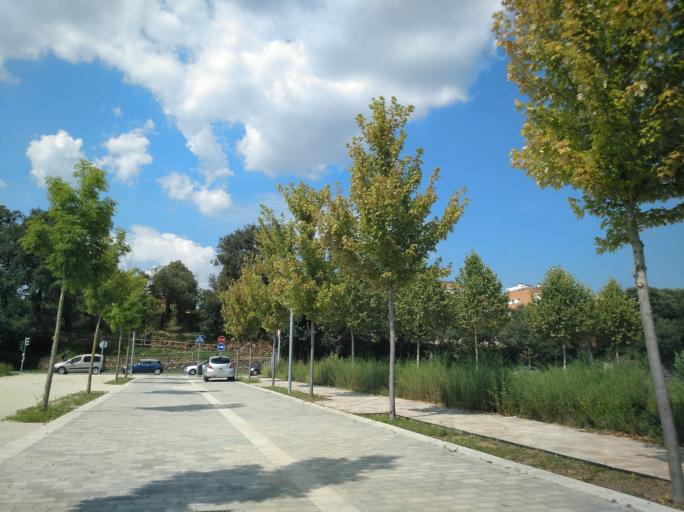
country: ES
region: Catalonia
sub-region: Provincia de Girona
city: Salt
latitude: 41.9912
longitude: 2.8024
